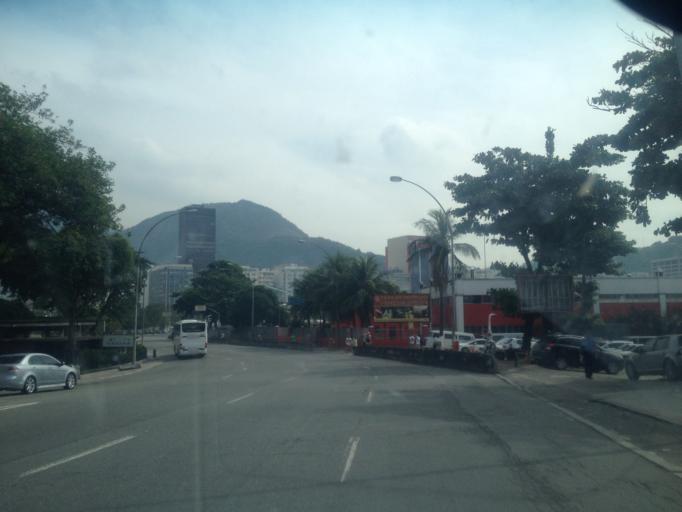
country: BR
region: Rio de Janeiro
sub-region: Rio De Janeiro
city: Rio de Janeiro
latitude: -22.9497
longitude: -43.1780
